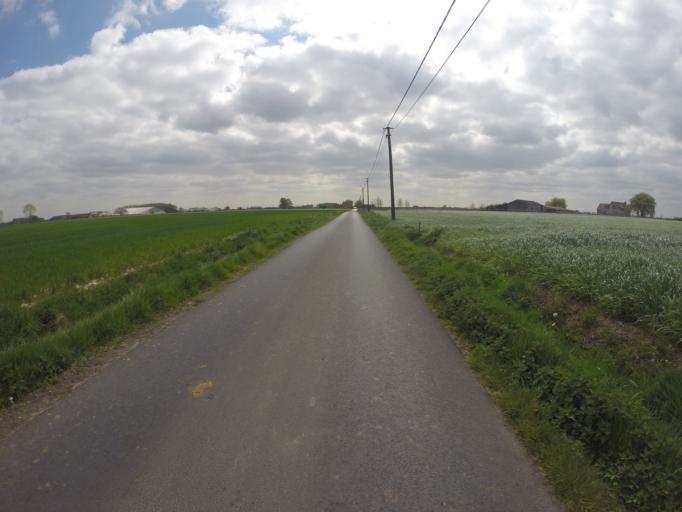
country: BE
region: Flanders
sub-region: Provincie Oost-Vlaanderen
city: Nevele
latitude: 51.0358
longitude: 3.4858
